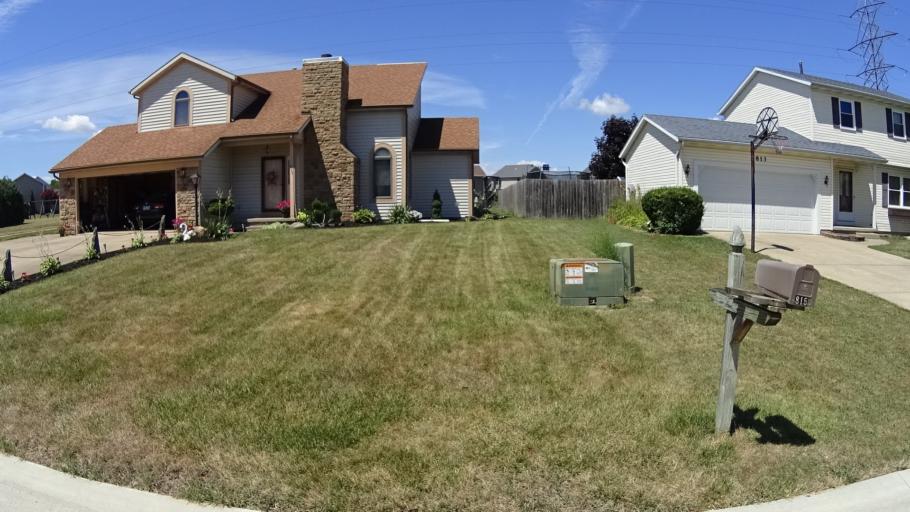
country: US
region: Ohio
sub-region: Erie County
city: Sandusky
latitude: 41.4035
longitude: -82.6925
